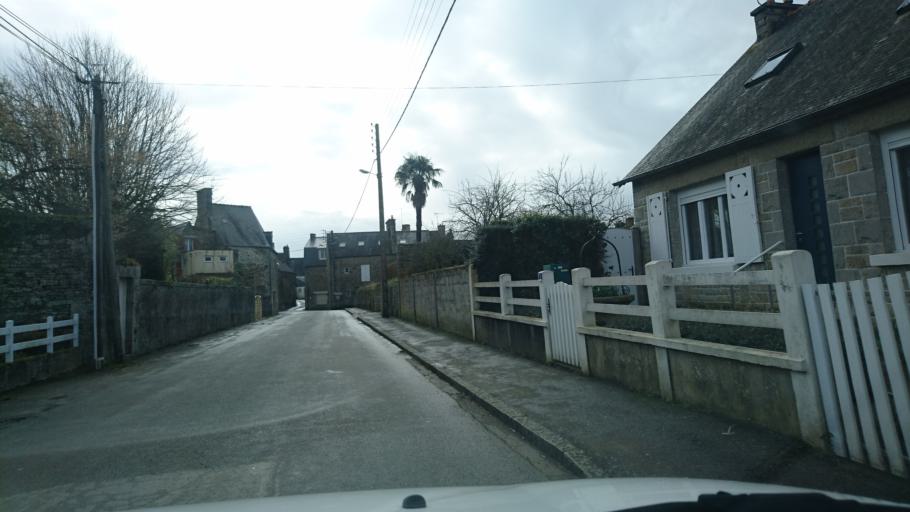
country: FR
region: Brittany
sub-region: Departement d'Ille-et-Vilaine
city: Antrain
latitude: 48.4622
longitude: -1.4868
